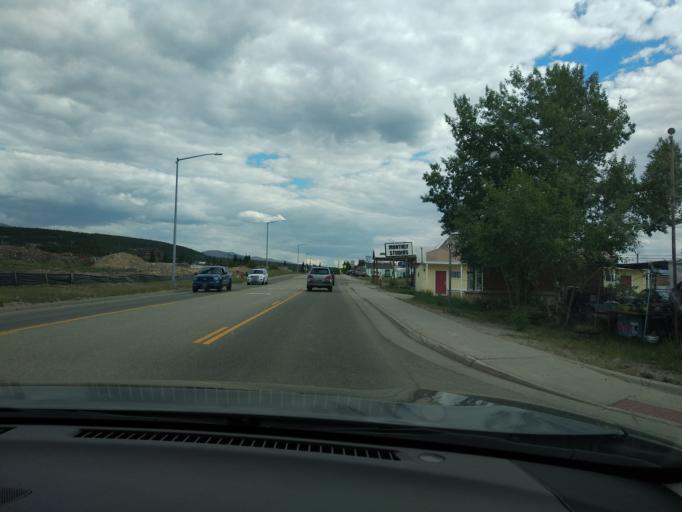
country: US
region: Colorado
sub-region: Lake County
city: Leadville
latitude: 39.2571
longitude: -106.2926
